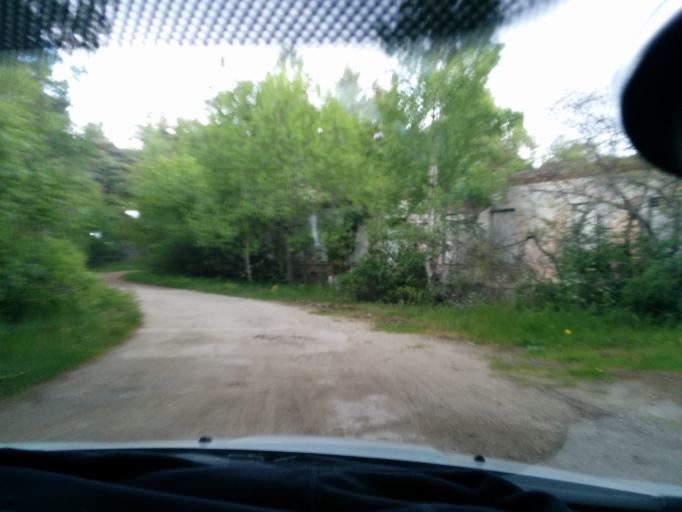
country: EE
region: Harju
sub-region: Loksa linn
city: Loksa
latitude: 59.6640
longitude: 25.7023
